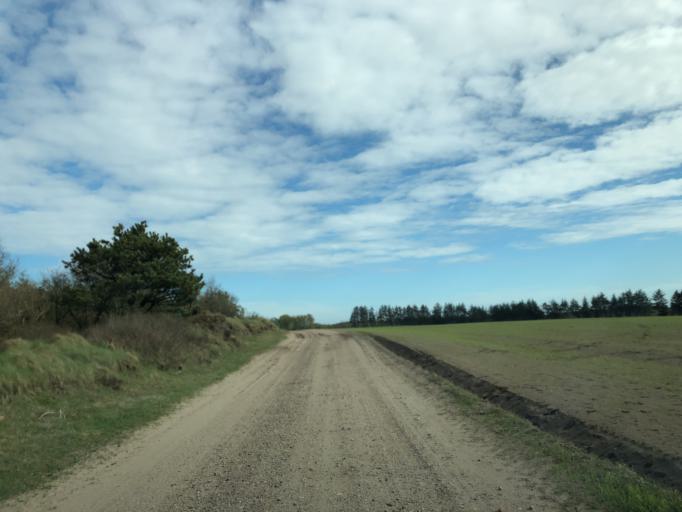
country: DK
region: Central Jutland
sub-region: Holstebro Kommune
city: Ulfborg
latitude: 56.2458
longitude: 8.3402
